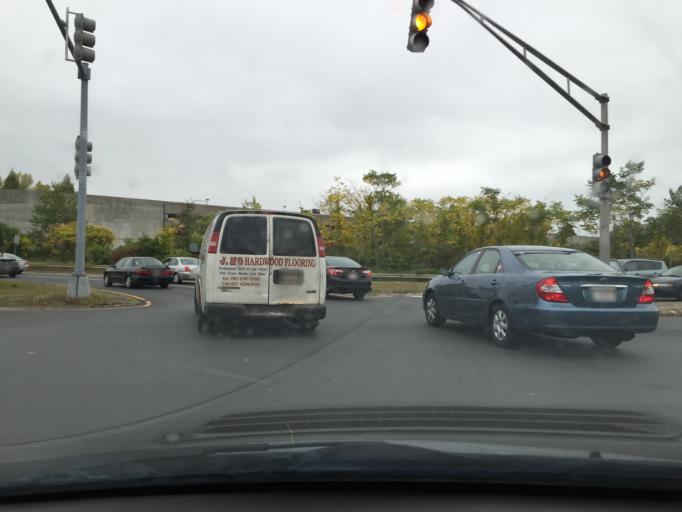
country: US
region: Massachusetts
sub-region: Middlesex County
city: Arlington
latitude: 42.3979
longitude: -71.1419
